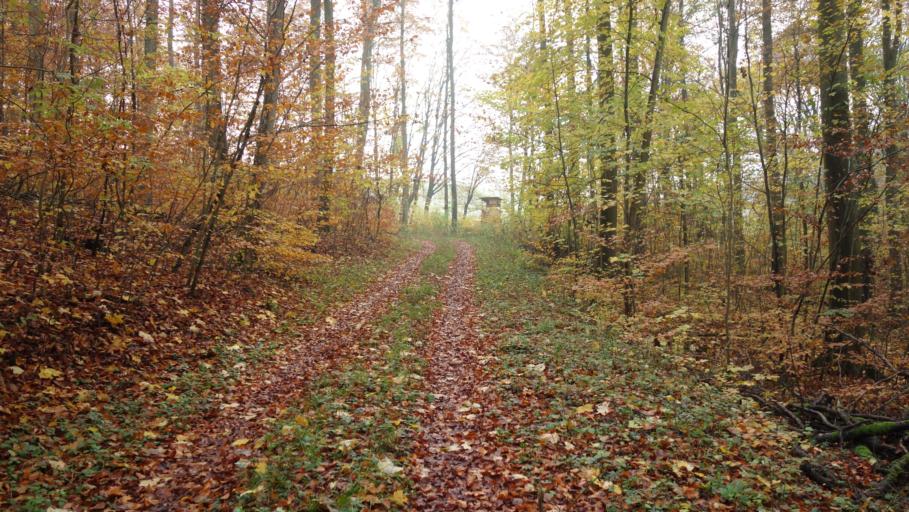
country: DE
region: Baden-Wuerttemberg
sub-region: Karlsruhe Region
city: Obrigheim
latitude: 49.3368
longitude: 9.0845
